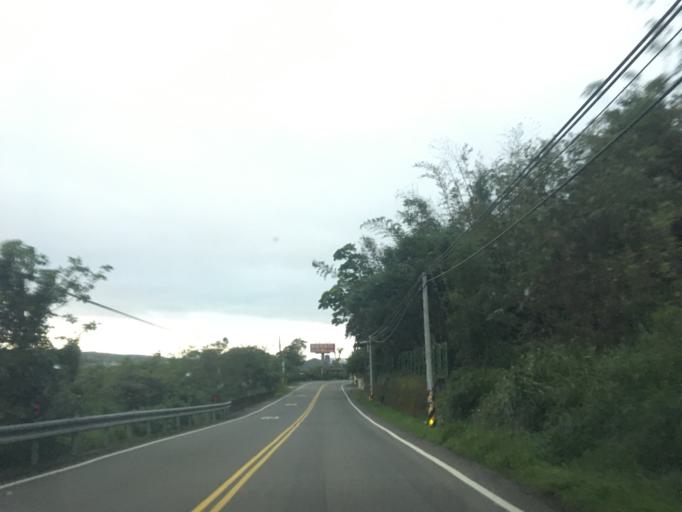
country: TW
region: Taiwan
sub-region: Miaoli
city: Miaoli
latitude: 24.4517
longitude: 120.7805
